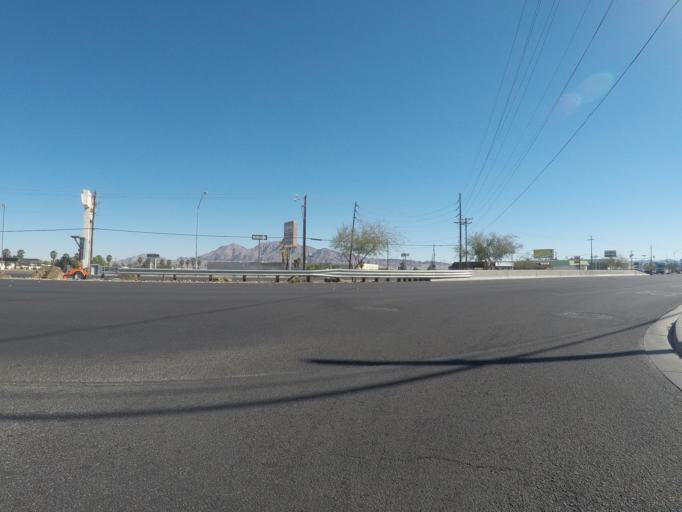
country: US
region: Nevada
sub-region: Clark County
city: Winchester
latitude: 36.1444
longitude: -115.1003
